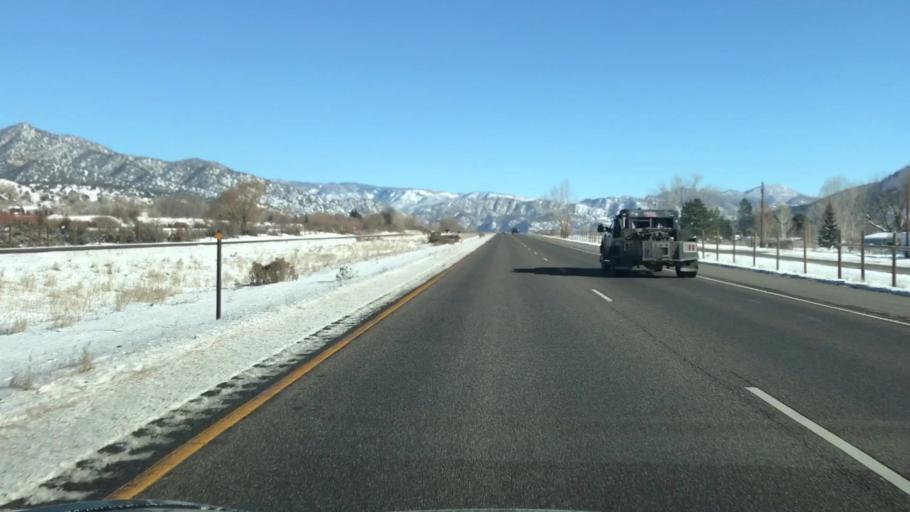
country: US
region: Colorado
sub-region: Garfield County
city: Silt
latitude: 39.5495
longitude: -107.6034
